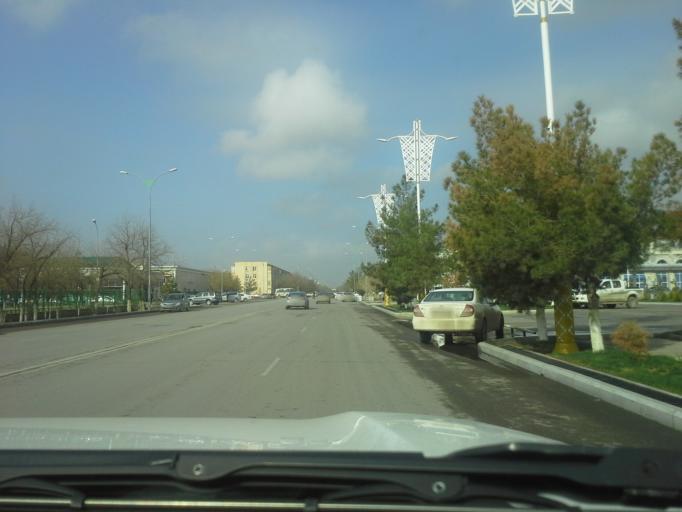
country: TM
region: Mary
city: Mary
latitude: 37.5917
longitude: 61.8362
